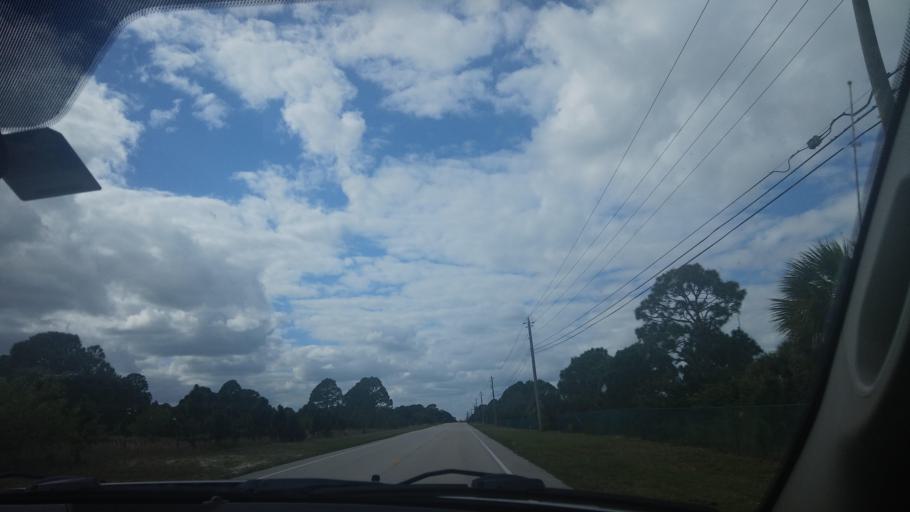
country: US
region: Florida
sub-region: Indian River County
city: Winter Beach
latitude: 27.7338
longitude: -80.4335
